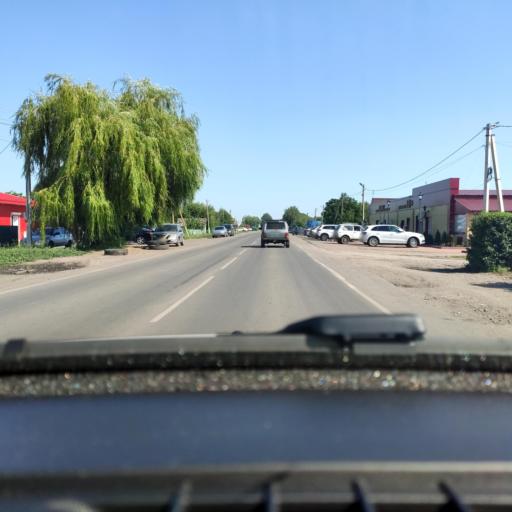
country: RU
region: Voronezj
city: Panino
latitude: 51.6574
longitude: 40.1251
